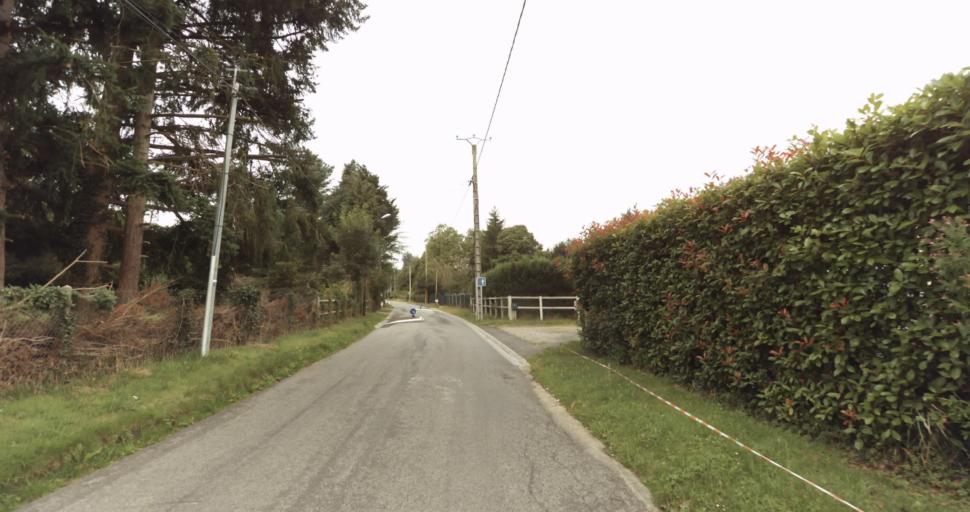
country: FR
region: Haute-Normandie
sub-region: Departement de l'Eure
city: Croth
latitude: 48.8710
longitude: 1.3640
